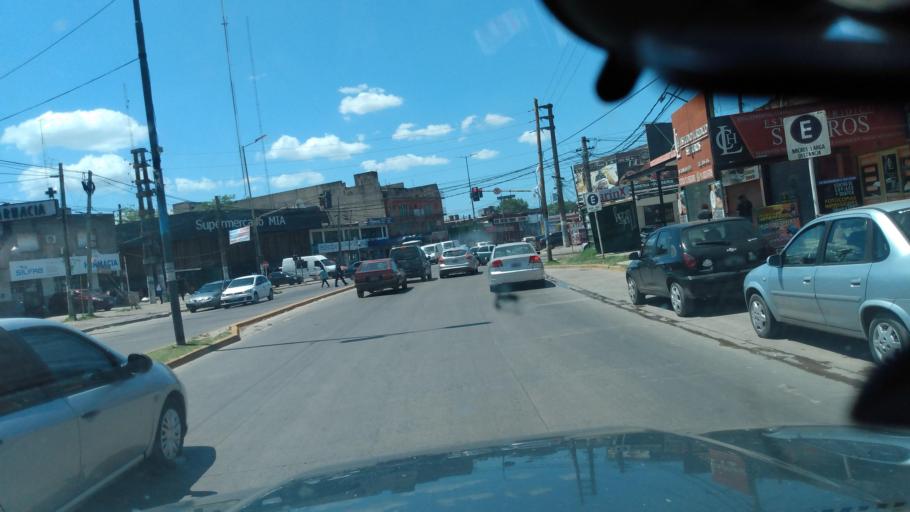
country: AR
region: Buenos Aires
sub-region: Partido de Merlo
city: Merlo
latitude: -34.5692
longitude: -58.7428
